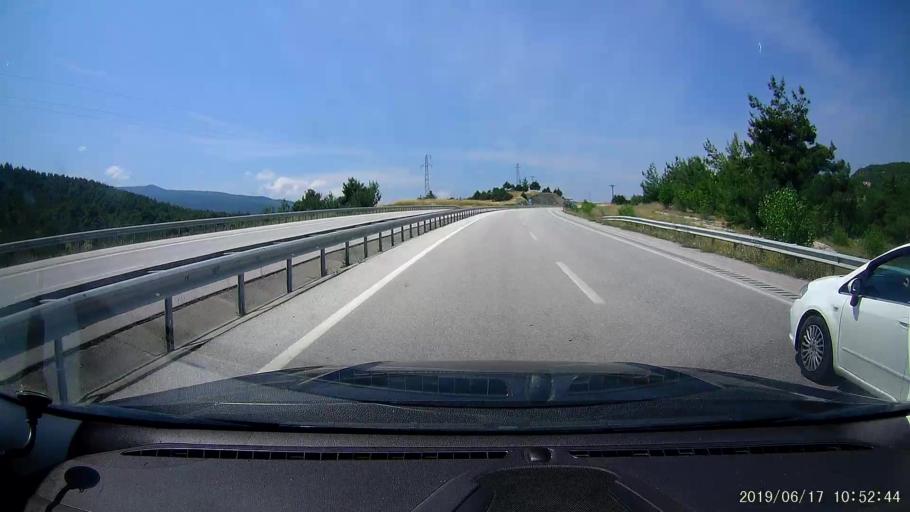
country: TR
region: Corum
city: Hacihamza
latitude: 41.0846
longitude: 34.3375
